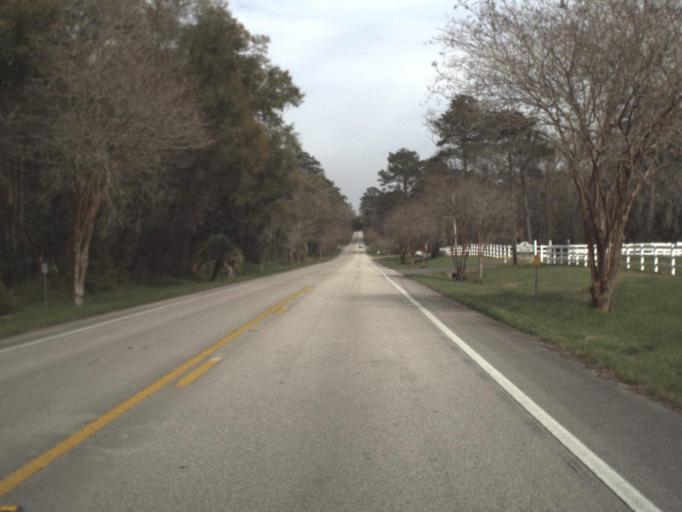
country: US
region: Florida
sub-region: Jefferson County
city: Monticello
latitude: 30.5324
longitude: -83.9551
